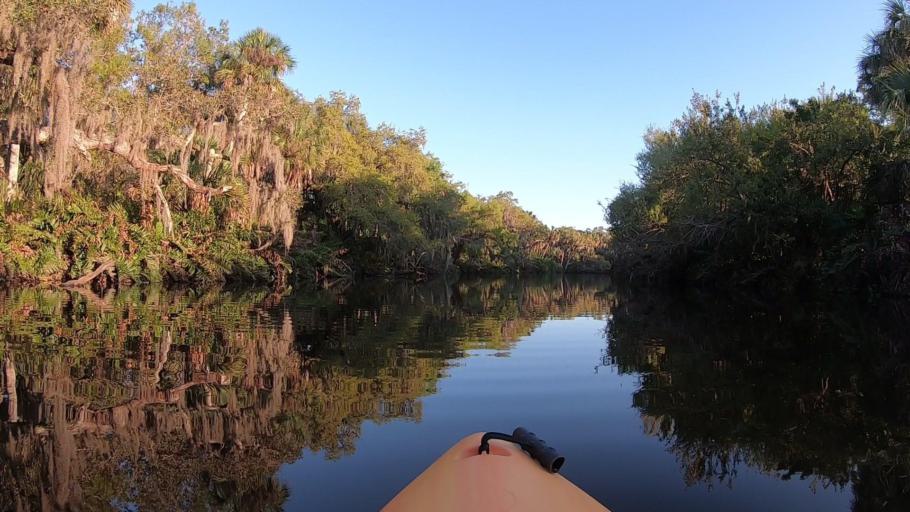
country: US
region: Florida
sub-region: Manatee County
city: Memphis
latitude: 27.5932
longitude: -82.5550
